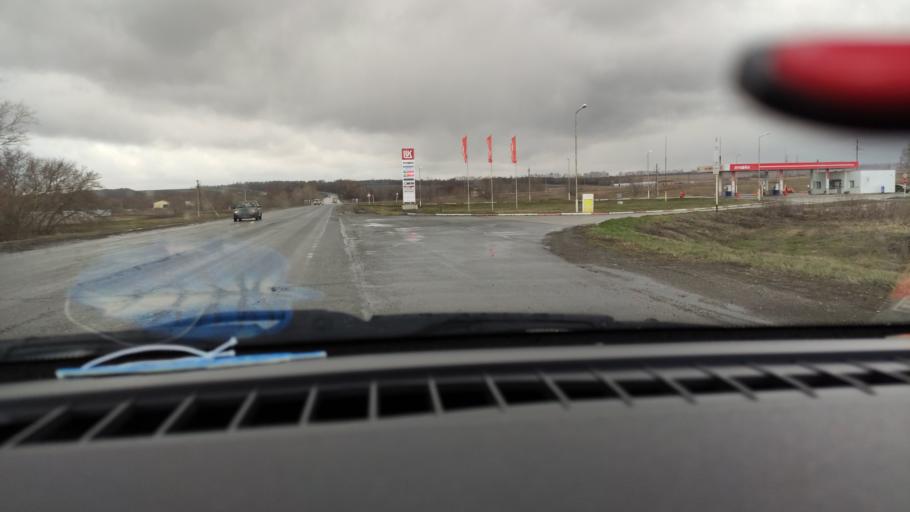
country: RU
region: Samara
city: Koshki
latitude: 54.1637
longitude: 50.4122
